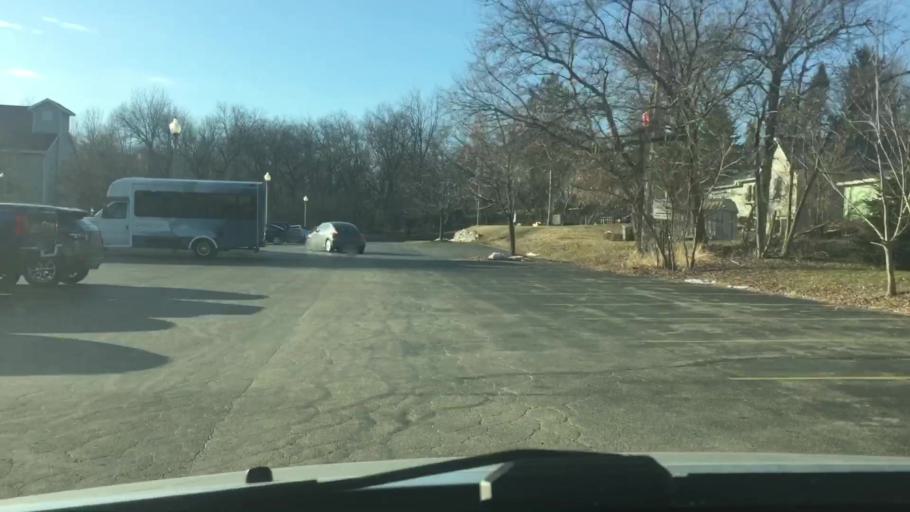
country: US
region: Wisconsin
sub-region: Waukesha County
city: Sussex
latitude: 43.1331
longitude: -88.2246
